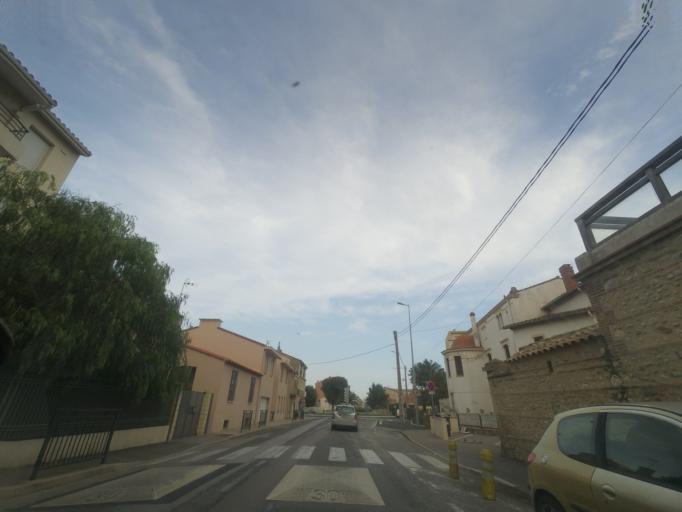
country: FR
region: Languedoc-Roussillon
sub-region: Departement des Pyrenees-Orientales
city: Perpignan
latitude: 42.6980
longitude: 2.8713
